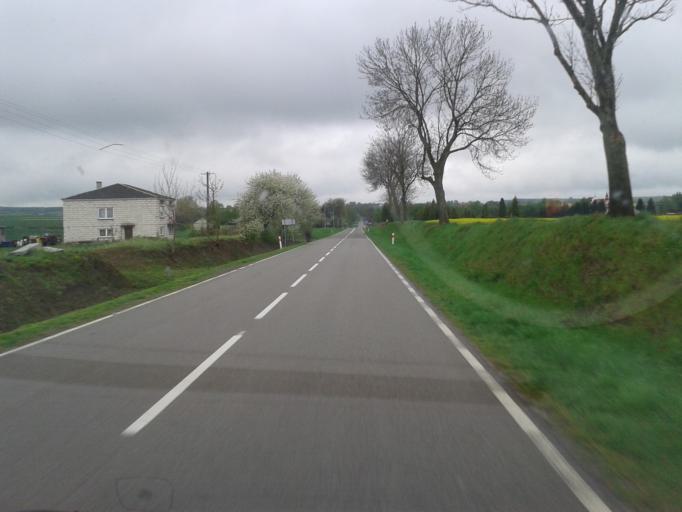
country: PL
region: Lublin Voivodeship
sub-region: Powiat tomaszowski
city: Telatyn
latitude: 50.5301
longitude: 23.9173
